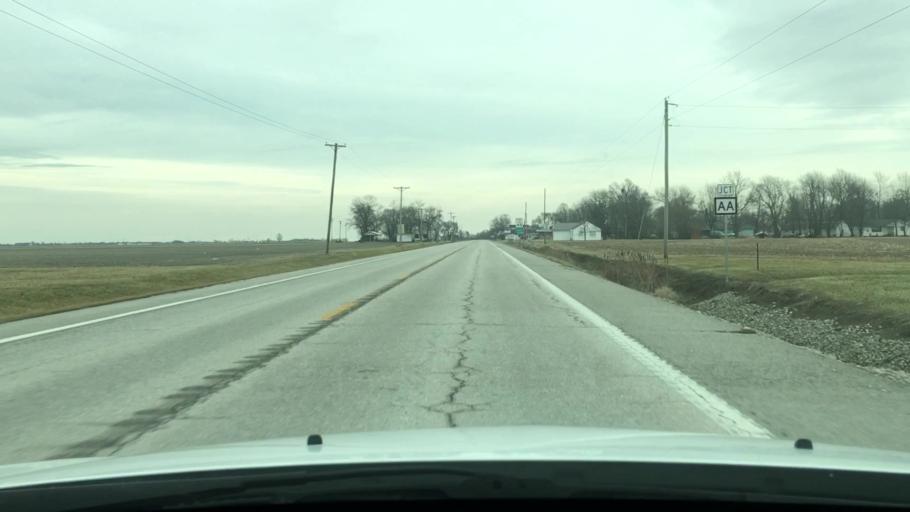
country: US
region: Missouri
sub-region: Audrain County
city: Vandalia
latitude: 39.2793
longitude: -91.5800
